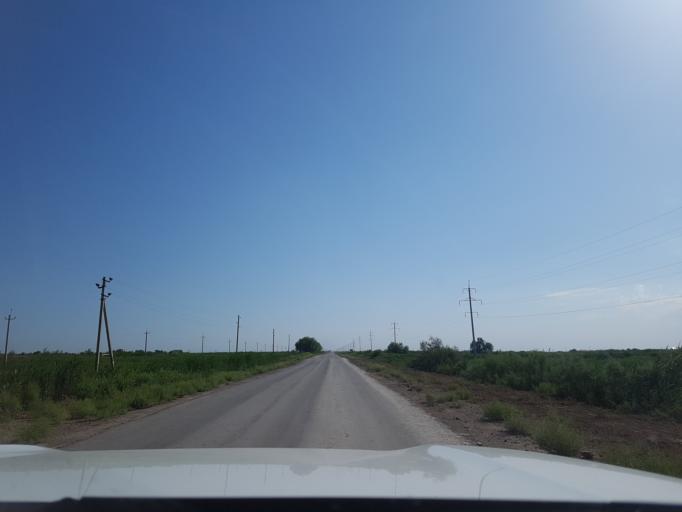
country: TM
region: Dasoguz
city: Koeneuergench
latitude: 42.1037
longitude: 58.9071
